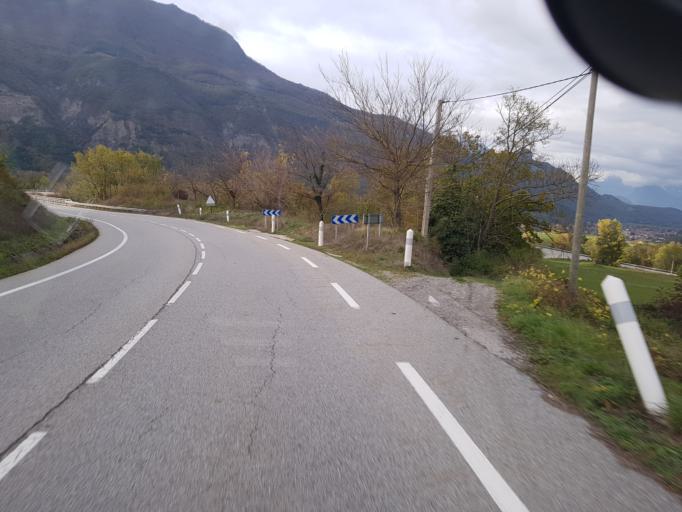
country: FR
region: Rhone-Alpes
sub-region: Departement de l'Isere
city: Vif
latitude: 45.0318
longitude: 5.6641
